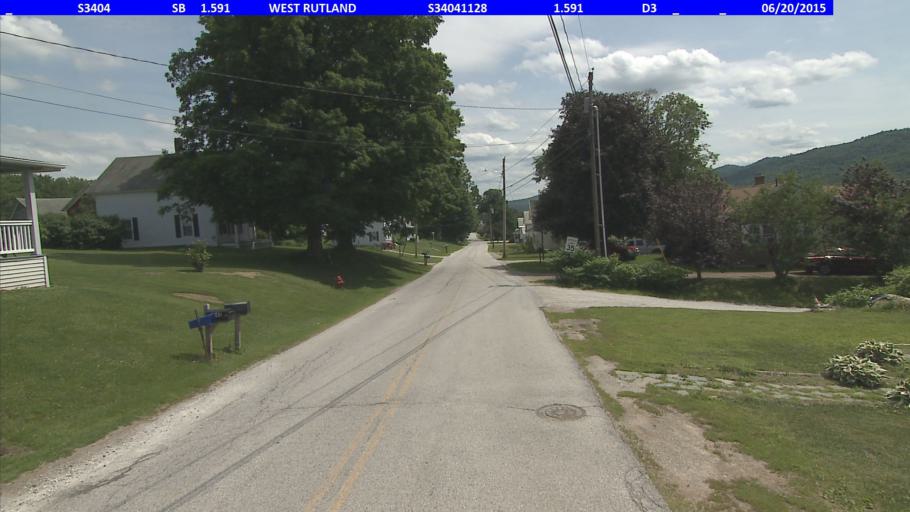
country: US
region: Vermont
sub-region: Rutland County
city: West Rutland
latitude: 43.6140
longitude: -73.0512
